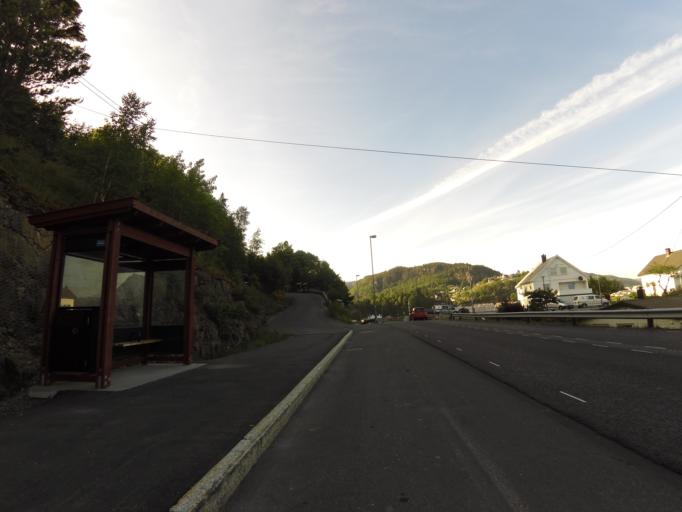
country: NO
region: Vest-Agder
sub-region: Flekkefjord
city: Flekkefjord
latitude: 58.2904
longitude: 6.6486
